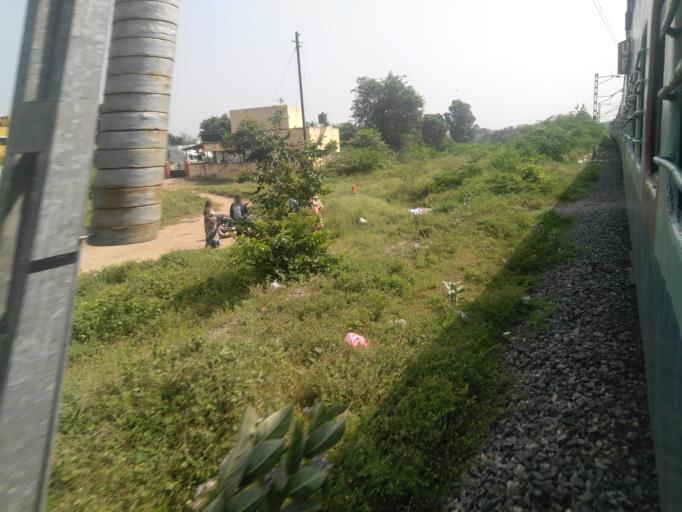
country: IN
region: Tamil Nadu
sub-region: Coimbatore
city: Mettupalayam
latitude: 11.2808
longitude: 76.9406
